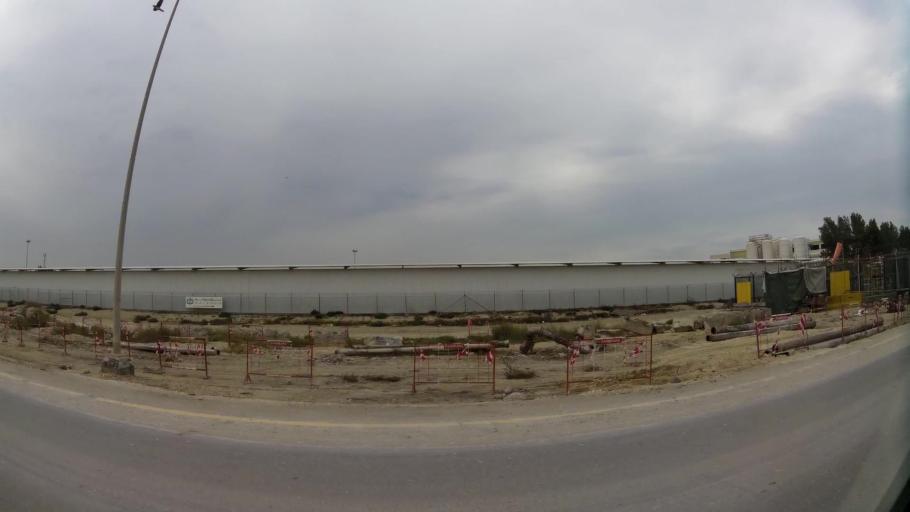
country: BH
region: Northern
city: Sitrah
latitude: 26.1789
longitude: 50.6216
